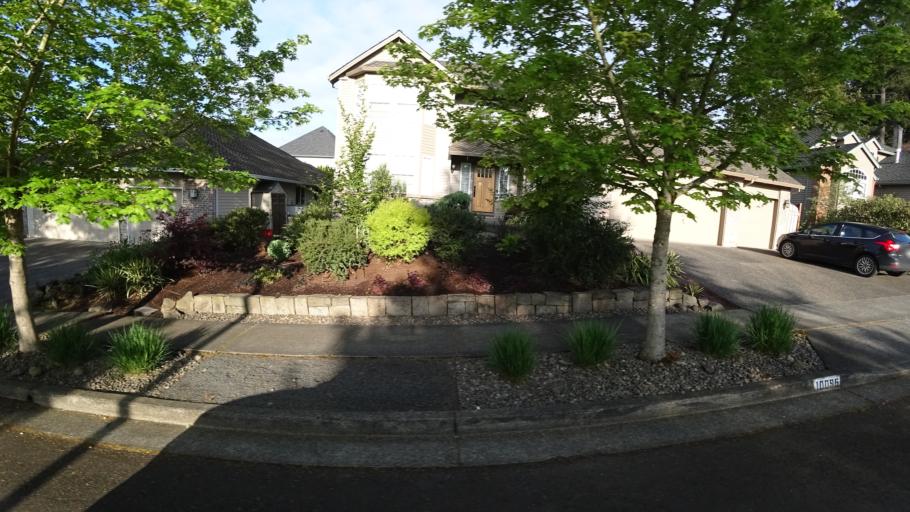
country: US
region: Oregon
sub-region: Washington County
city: Beaverton
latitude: 45.4470
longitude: -122.8230
